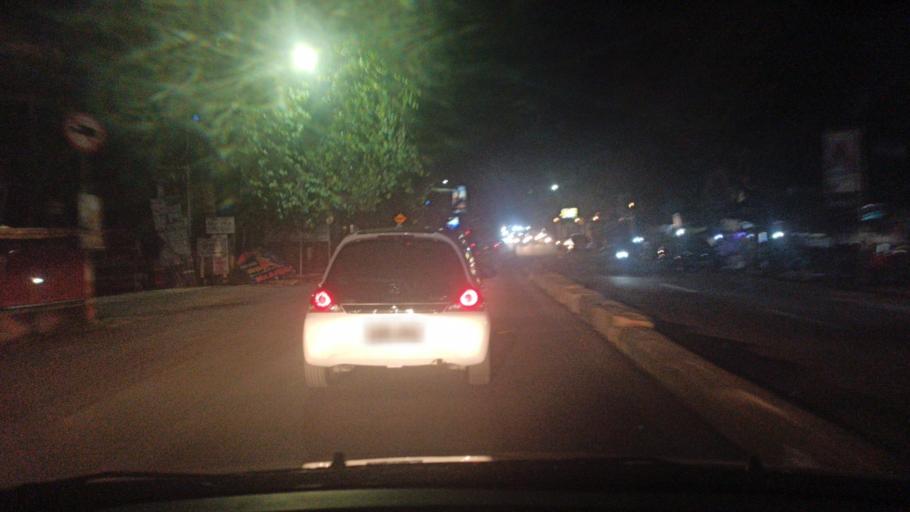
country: ID
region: South Sumatra
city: Palembang
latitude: -2.9803
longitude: 104.7242
